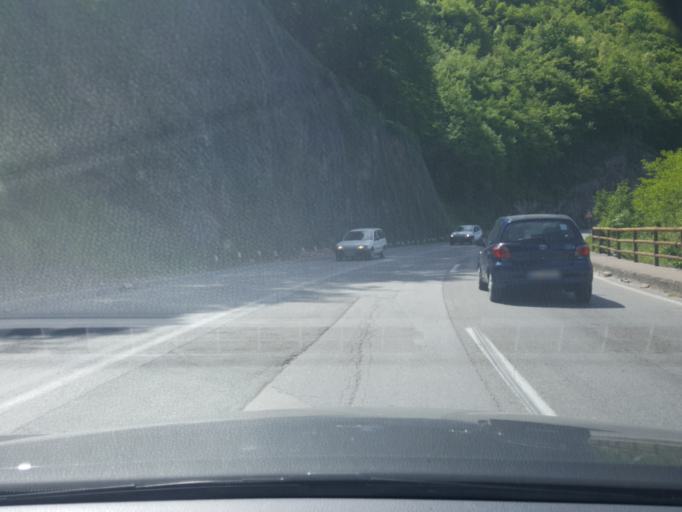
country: RS
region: Central Serbia
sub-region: Zlatiborski Okrug
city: Uzice
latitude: 43.8495
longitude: 19.8249
